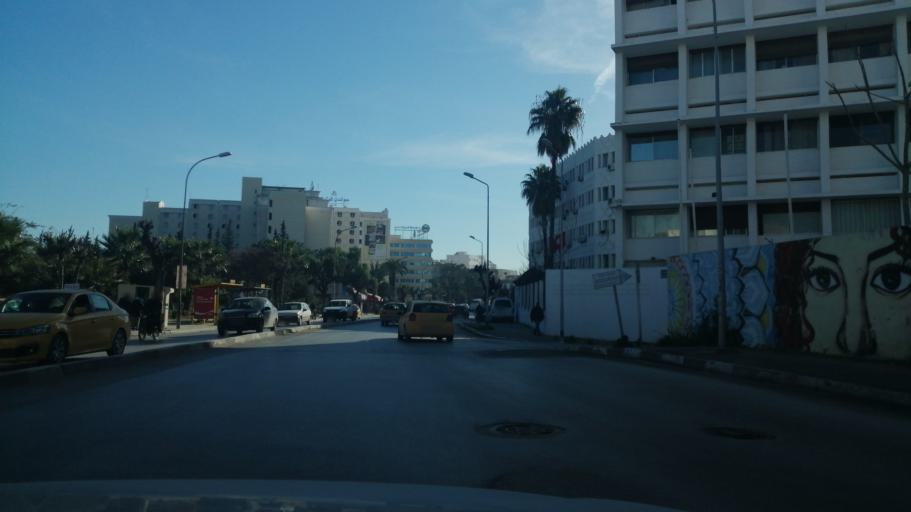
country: TN
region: Tunis
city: Tunis
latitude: 36.8136
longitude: 10.1713
